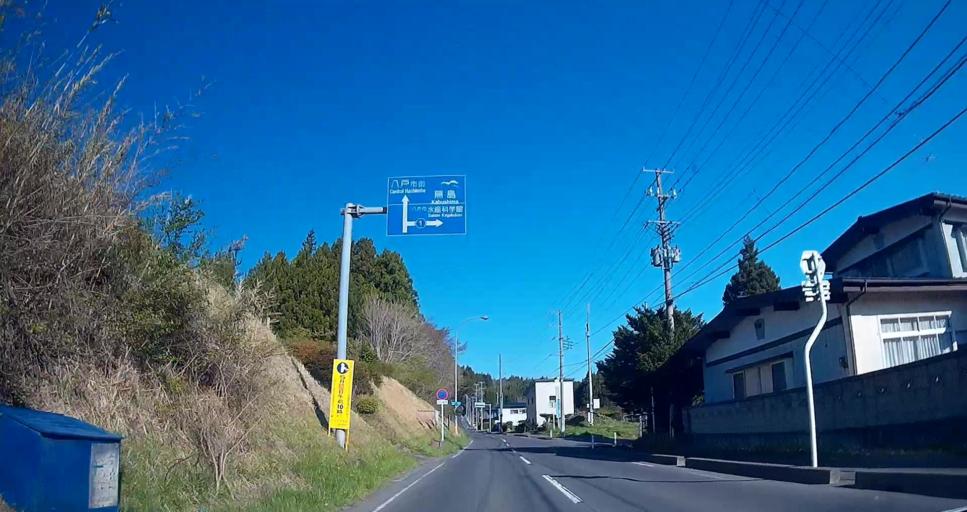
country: JP
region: Aomori
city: Hachinohe
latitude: 40.5175
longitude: 141.5856
